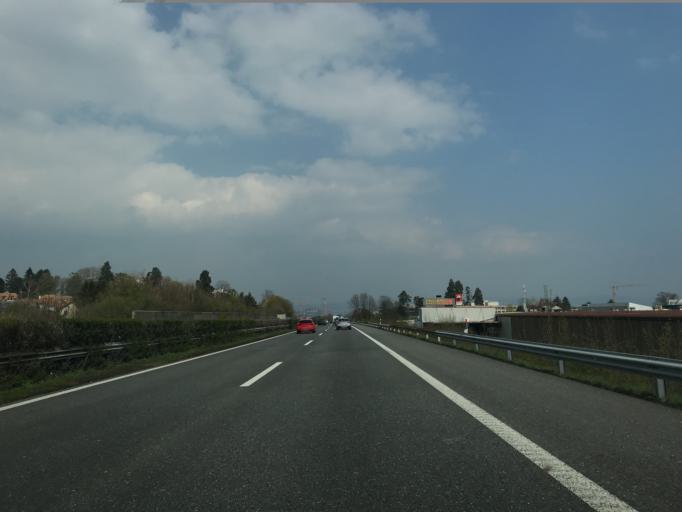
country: CH
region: Vaud
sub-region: Morges District
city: Morges
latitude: 46.5012
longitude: 6.4765
